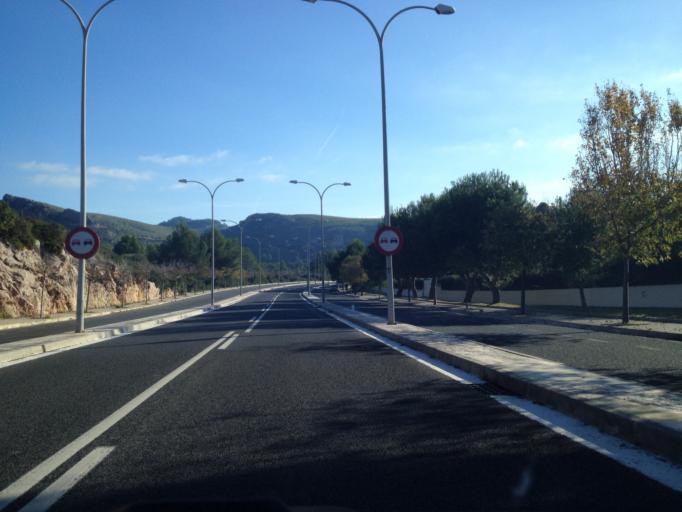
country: ES
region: Balearic Islands
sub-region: Illes Balears
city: Alcudia
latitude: 39.9137
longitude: 3.0927
